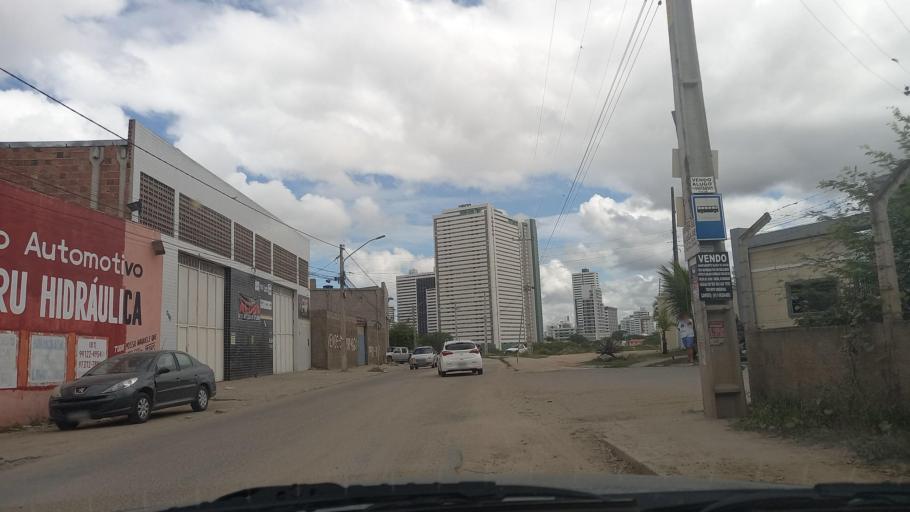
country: BR
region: Pernambuco
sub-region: Caruaru
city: Caruaru
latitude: -8.2626
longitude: -35.9590
